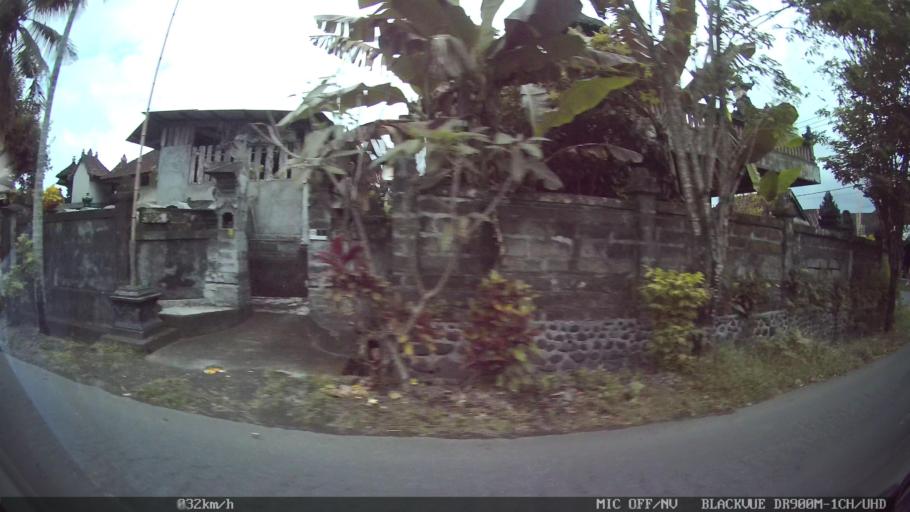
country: ID
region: Bali
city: Banjar Pekenjelodan
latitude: -8.5667
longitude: 115.1827
